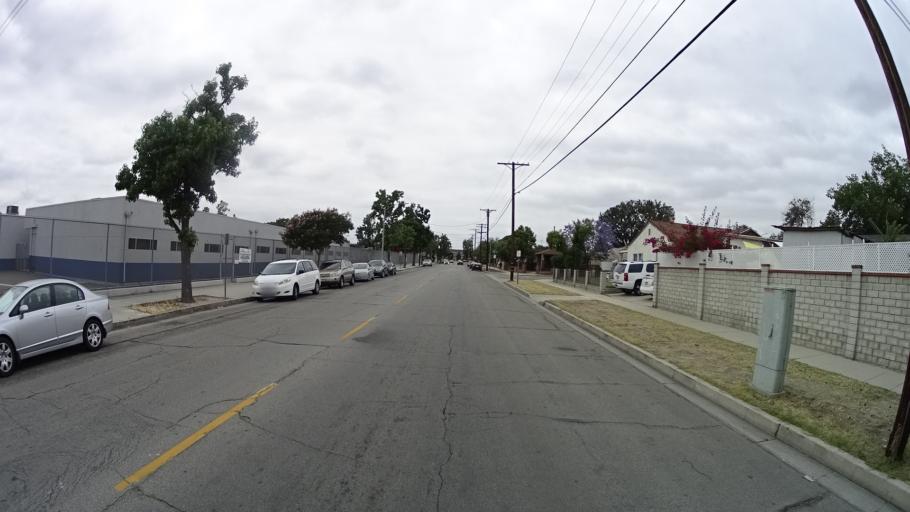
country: US
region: California
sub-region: Los Angeles County
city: Burbank
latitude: 34.1992
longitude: -118.3339
